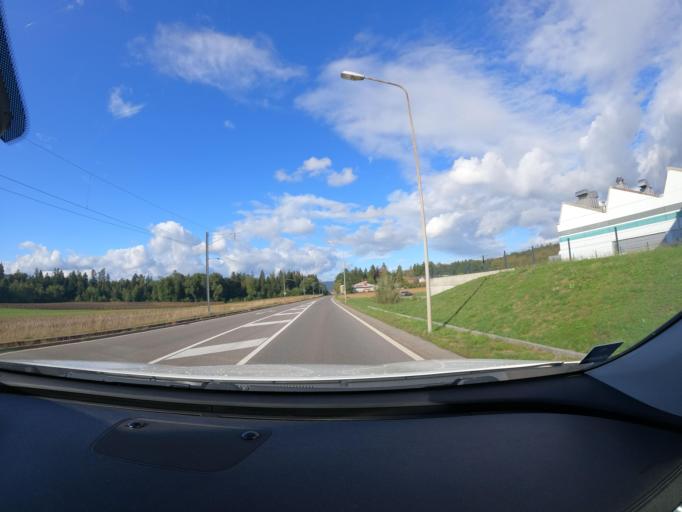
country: CH
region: Aargau
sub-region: Bezirk Lenzburg
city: Seon
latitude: 47.3631
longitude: 8.1645
